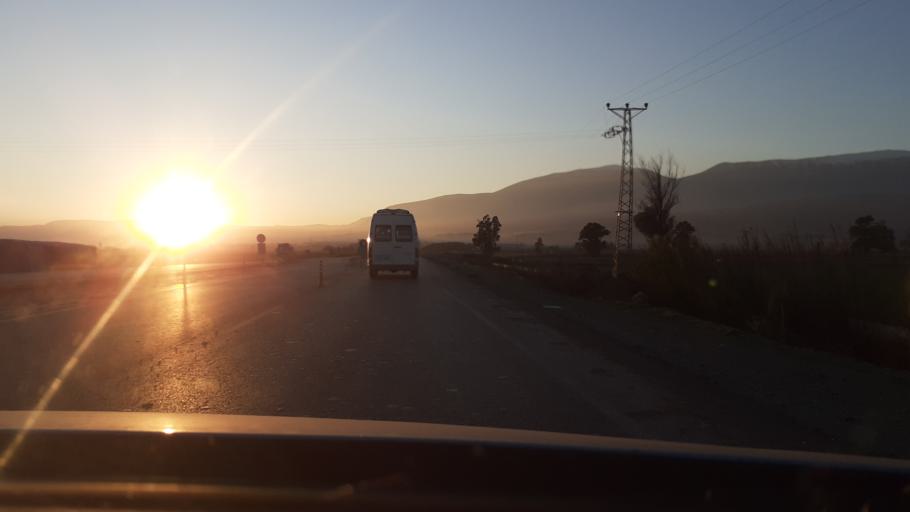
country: TR
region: Hatay
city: Kirikhan
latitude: 36.5047
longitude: 36.4116
